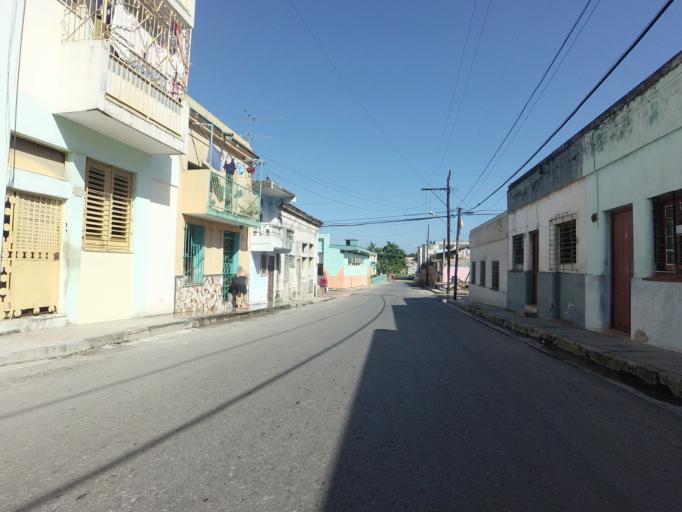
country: CU
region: La Habana
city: Cerro
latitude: 23.1203
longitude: -82.3740
